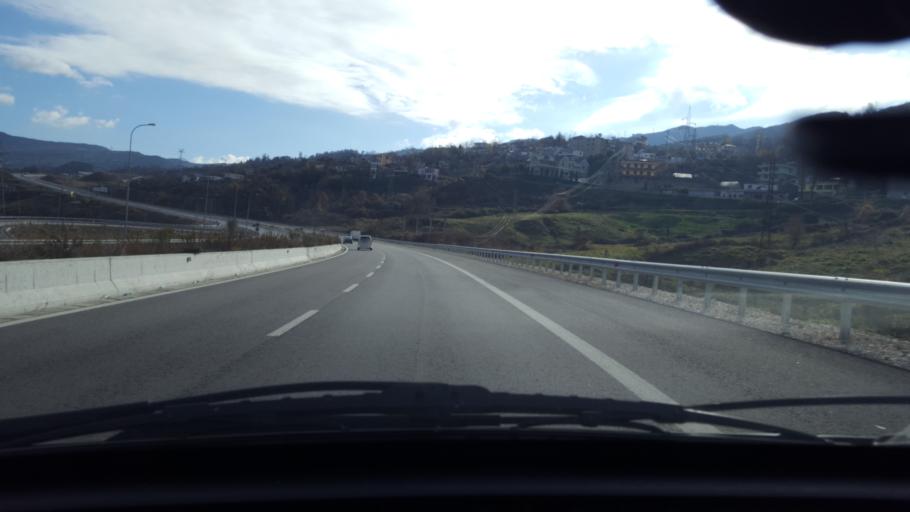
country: AL
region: Tirane
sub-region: Rrethi i Tiranes
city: Berzhite
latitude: 41.2293
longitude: 19.9300
